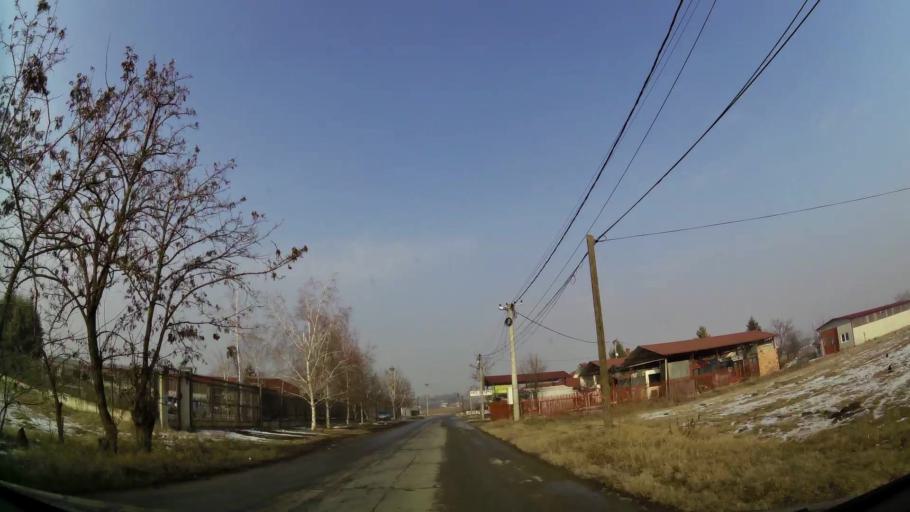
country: MK
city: Kadino
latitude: 41.9749
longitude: 21.5980
